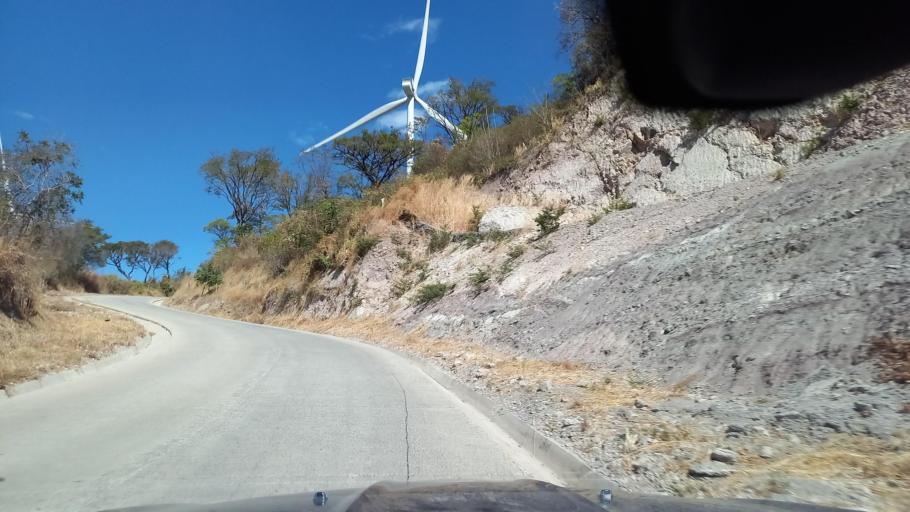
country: SV
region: Santa Ana
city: Metapan
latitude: 14.3663
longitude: -89.4849
